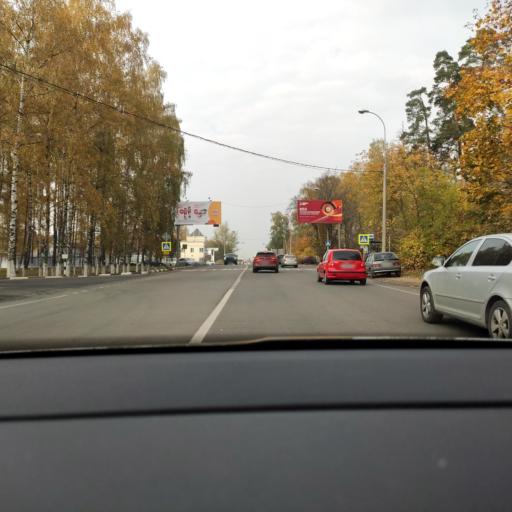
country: RU
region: Moskovskaya
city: Lesnyye Polyany
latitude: 55.9829
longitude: 37.8864
